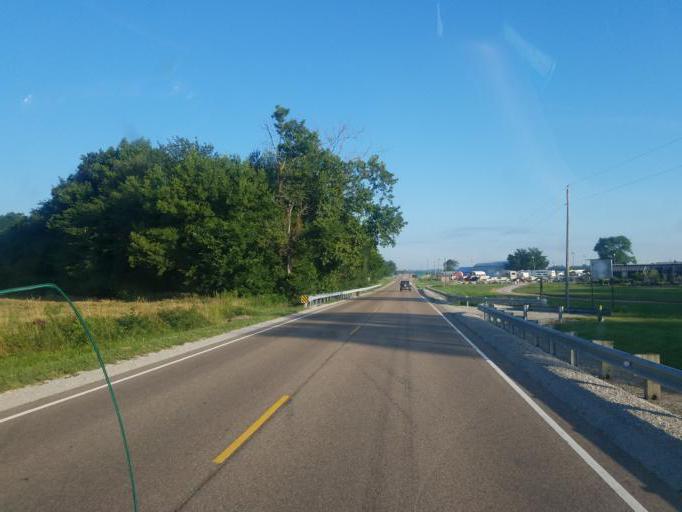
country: US
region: Illinois
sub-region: Bond County
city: Greenville
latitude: 38.8651
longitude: -89.3781
